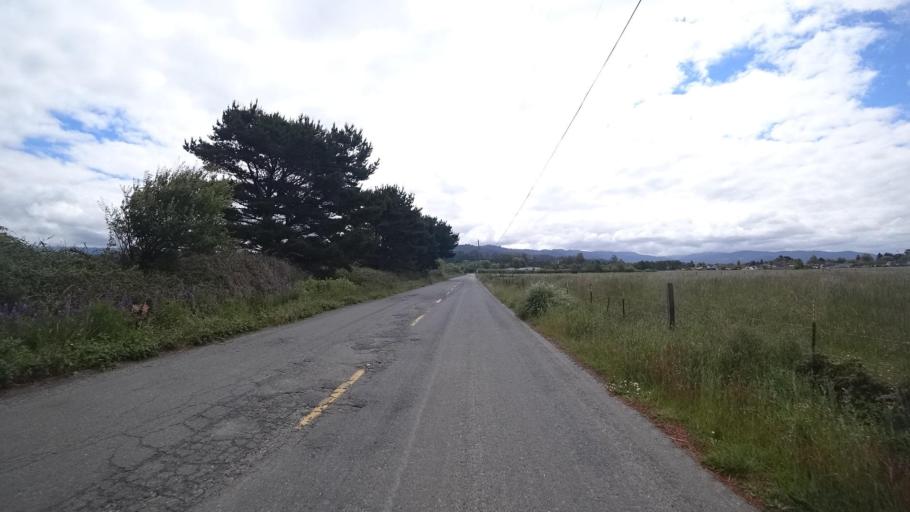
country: US
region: California
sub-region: Humboldt County
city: Arcata
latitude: 40.8808
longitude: -124.0993
